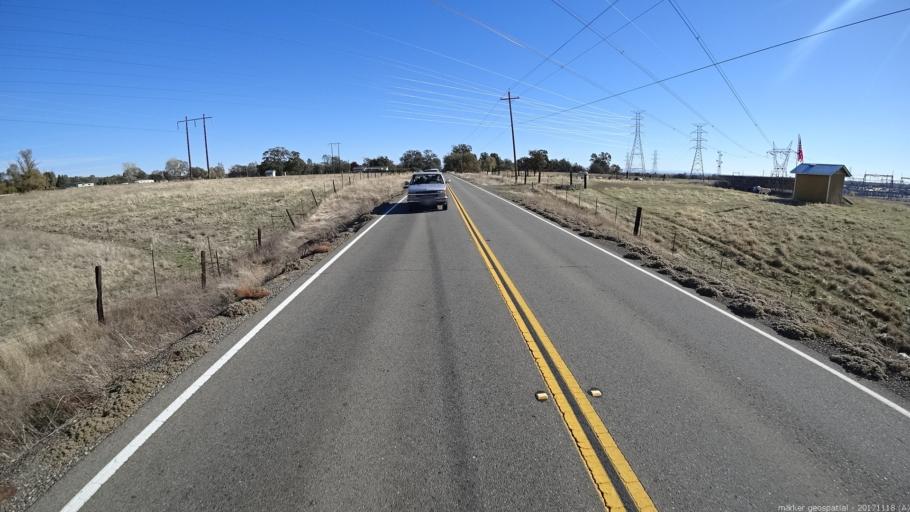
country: US
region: California
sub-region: Shasta County
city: Cottonwood
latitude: 40.3887
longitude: -122.3862
